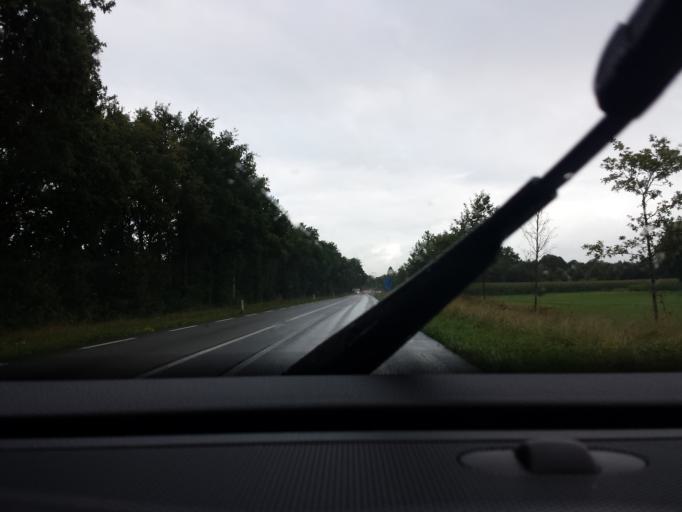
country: NL
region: Gelderland
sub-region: Gemeente Lochem
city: Laren
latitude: 52.1957
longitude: 6.3703
